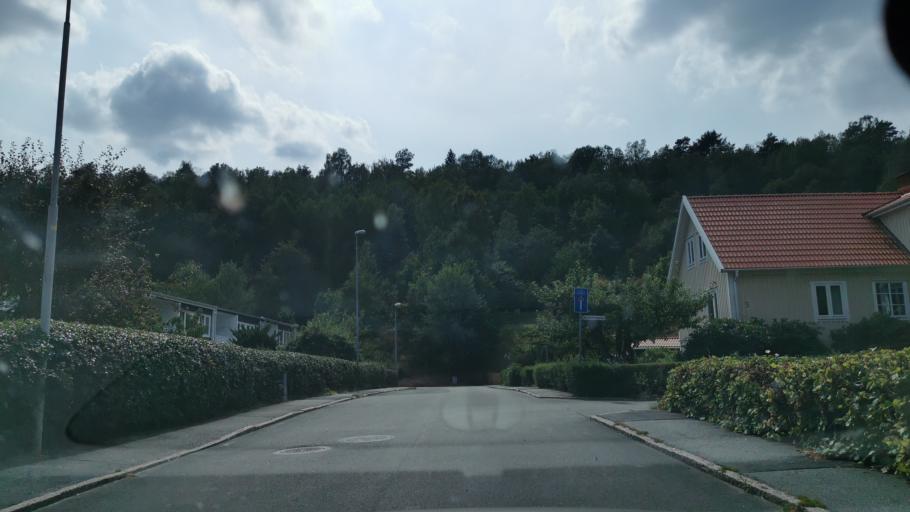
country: SE
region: Vaestra Goetaland
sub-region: Molndal
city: Moelndal
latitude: 57.6698
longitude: 11.9806
